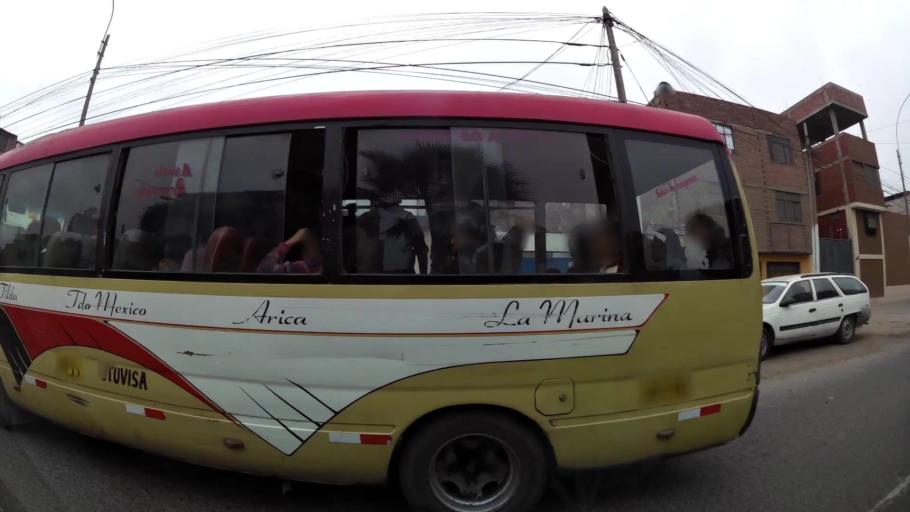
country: PE
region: Callao
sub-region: Callao
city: Callao
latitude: -12.0537
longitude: -77.1177
